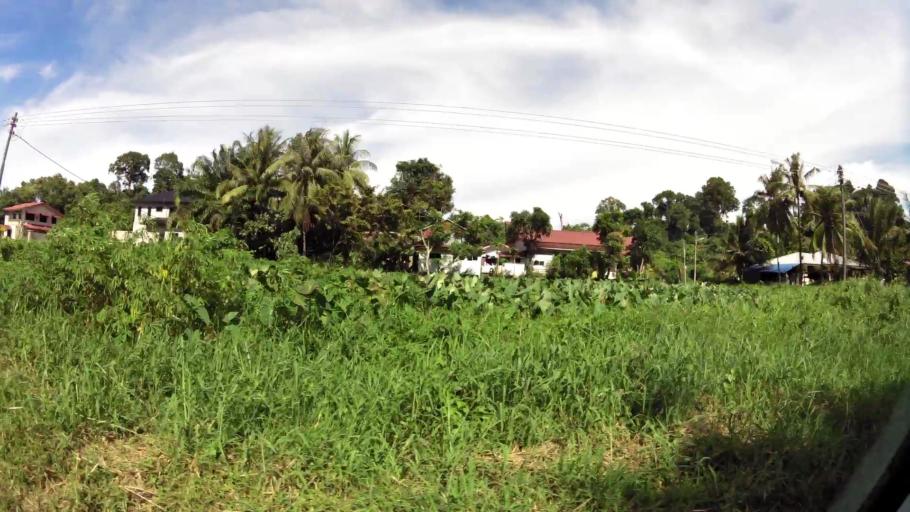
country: BN
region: Brunei and Muara
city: Bandar Seri Begawan
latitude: 5.0296
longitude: 115.0445
